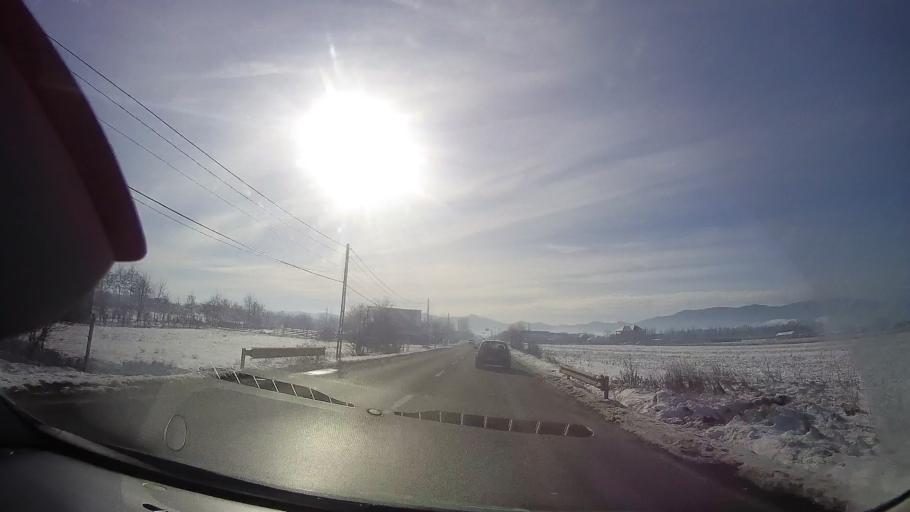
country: RO
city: Vanatori-Neamt
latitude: 47.1770
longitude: 26.3277
